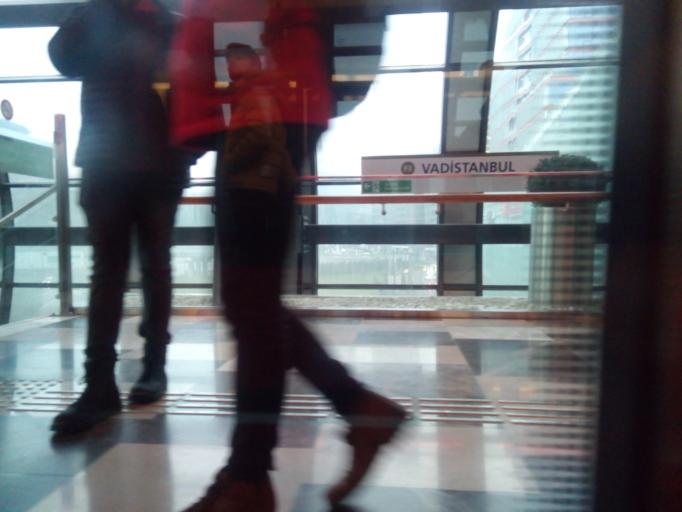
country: TR
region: Istanbul
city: Sisli
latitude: 41.1081
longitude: 28.9886
